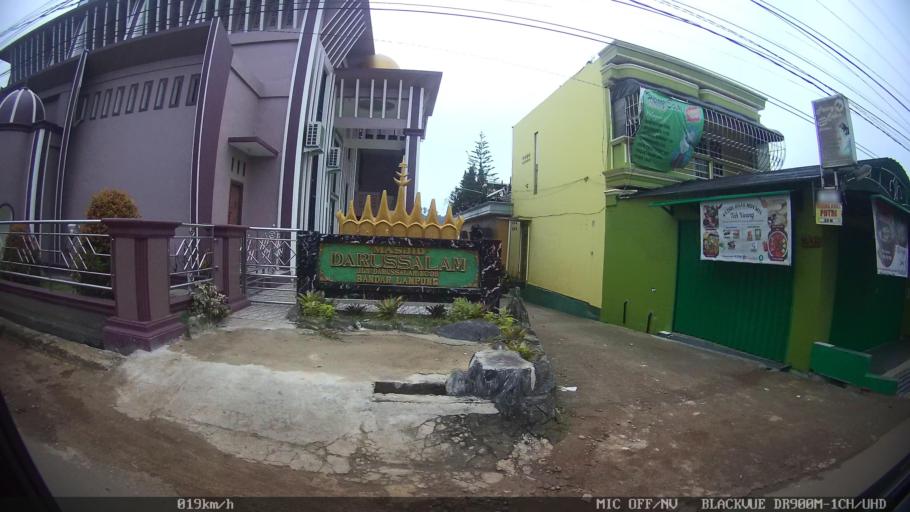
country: ID
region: Lampung
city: Kedaton
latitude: -5.3959
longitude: 105.2333
